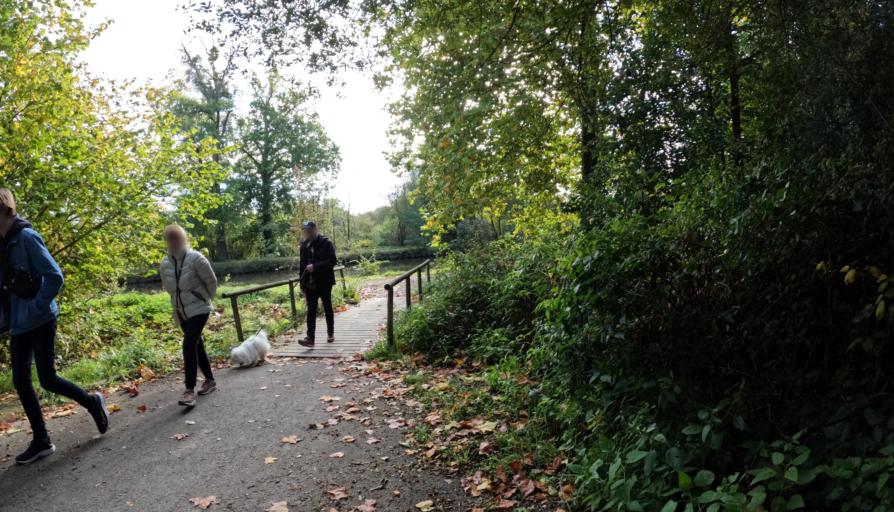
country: FR
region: Brittany
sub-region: Departement d'Ille-et-Vilaine
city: Betton
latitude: 48.1848
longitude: -1.6384
